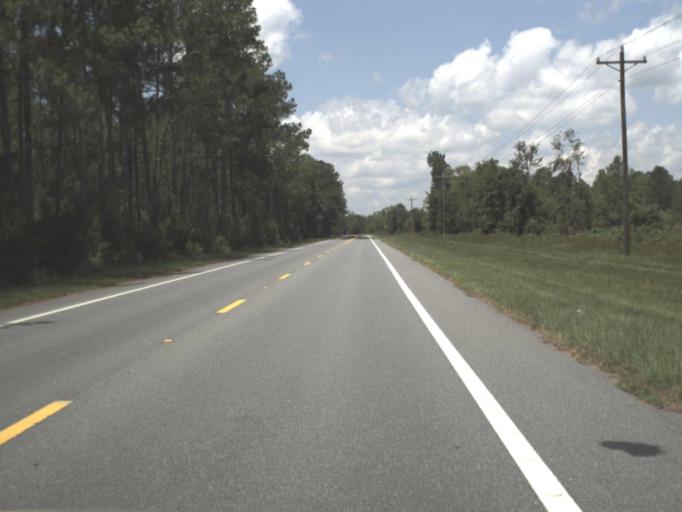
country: US
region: Florida
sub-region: Union County
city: Lake Butler
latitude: 30.0077
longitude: -82.4735
